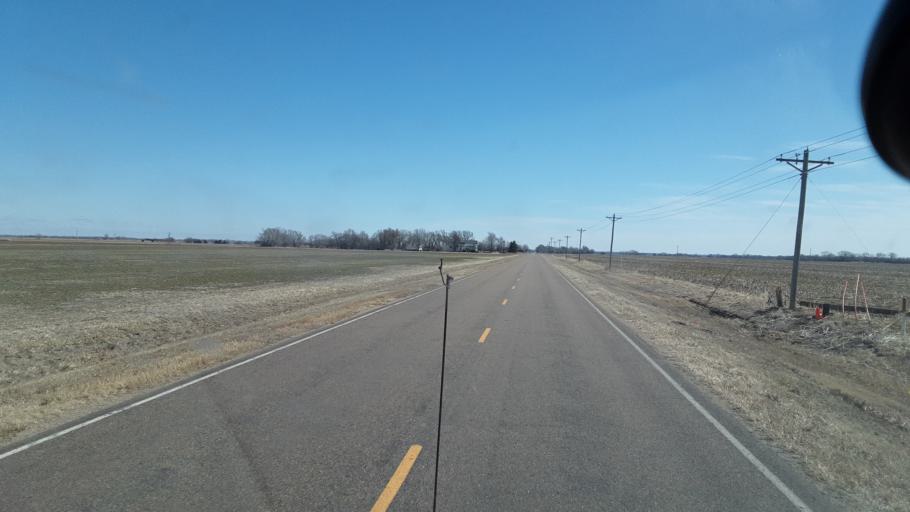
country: US
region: Kansas
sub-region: Rice County
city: Sterling
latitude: 38.2176
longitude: -98.1482
